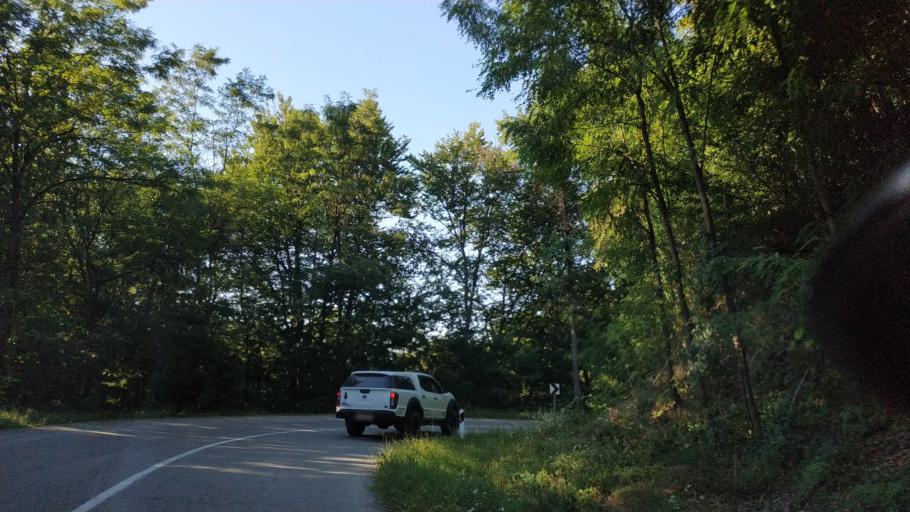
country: RS
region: Central Serbia
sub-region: Rasinski Okrug
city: Krusevac
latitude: 43.4616
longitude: 21.3603
